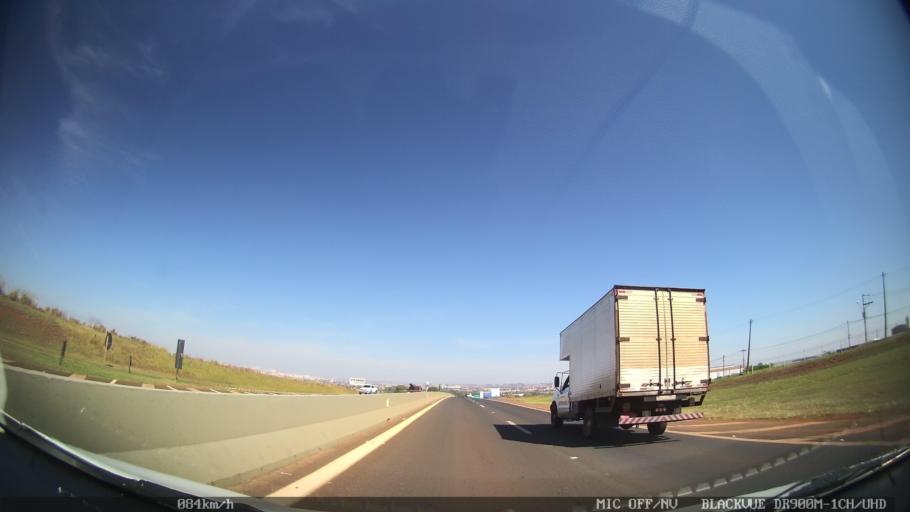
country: BR
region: Sao Paulo
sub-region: Jardinopolis
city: Jardinopolis
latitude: -21.0950
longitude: -47.7959
